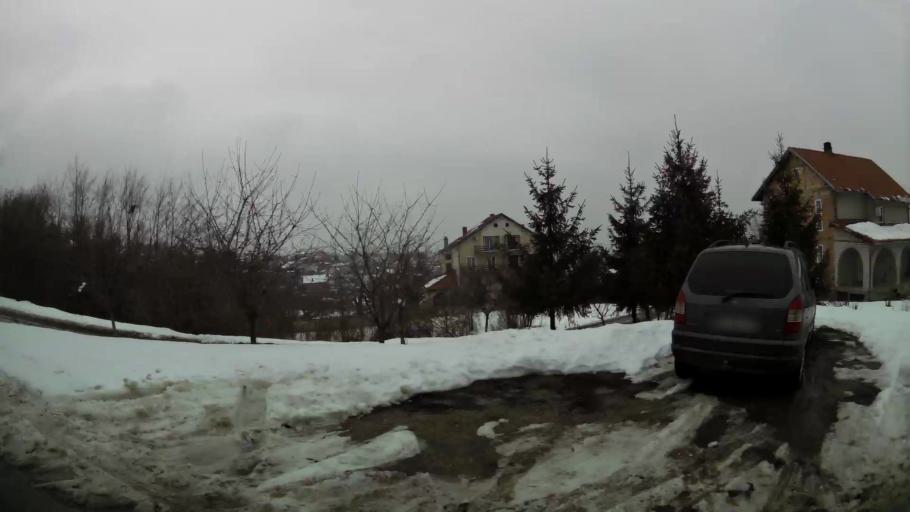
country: RS
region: Central Serbia
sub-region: Belgrade
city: Zvezdara
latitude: 44.7408
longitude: 20.5101
